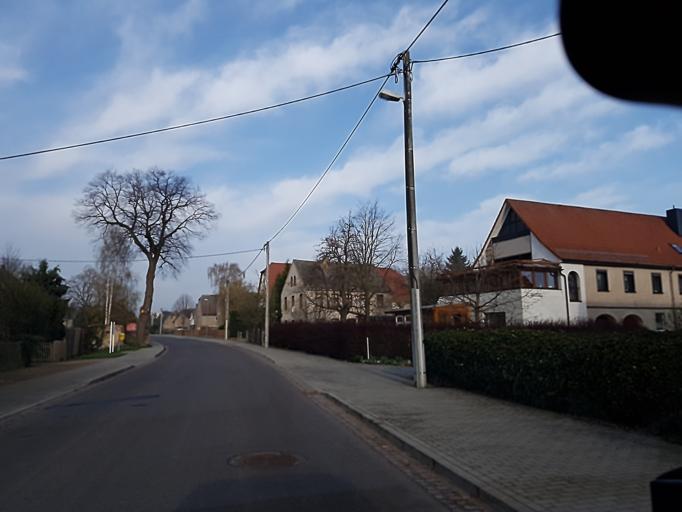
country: DE
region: Saxony
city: Naundorf
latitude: 51.2569
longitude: 13.1390
